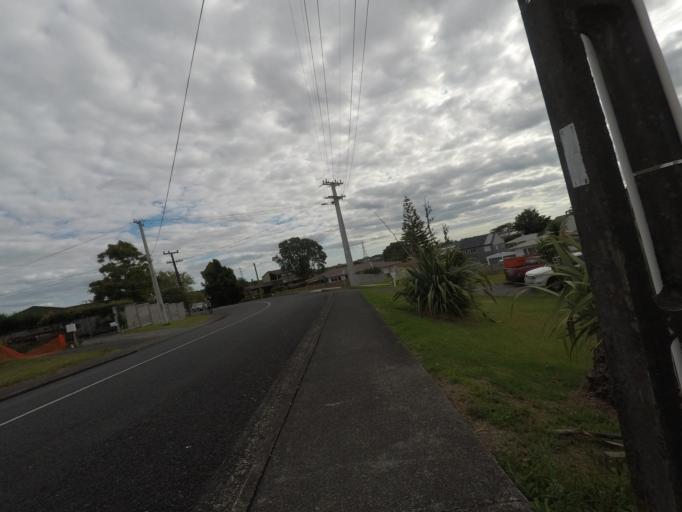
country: NZ
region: Auckland
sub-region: Auckland
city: Papakura
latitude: -37.0584
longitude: 174.9319
